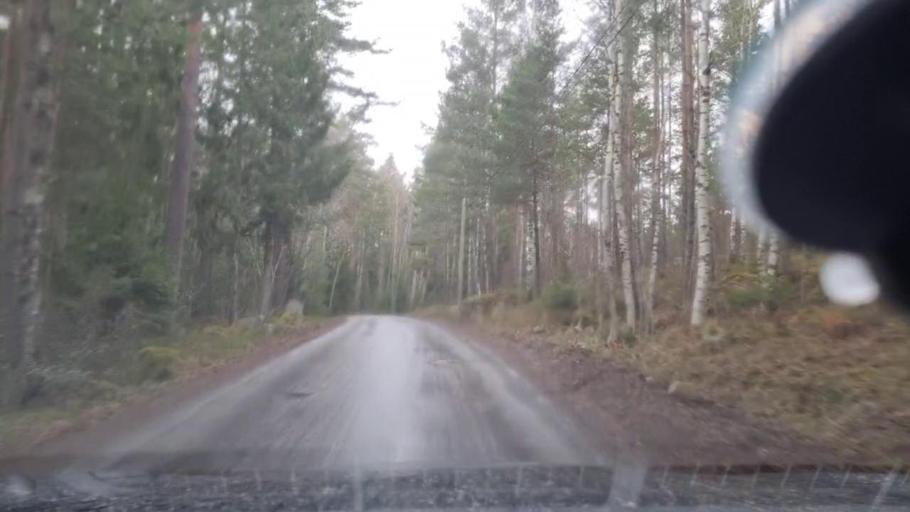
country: SE
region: Stockholm
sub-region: Vallentuna Kommun
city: Vallentuna
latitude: 59.5098
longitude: 18.0097
